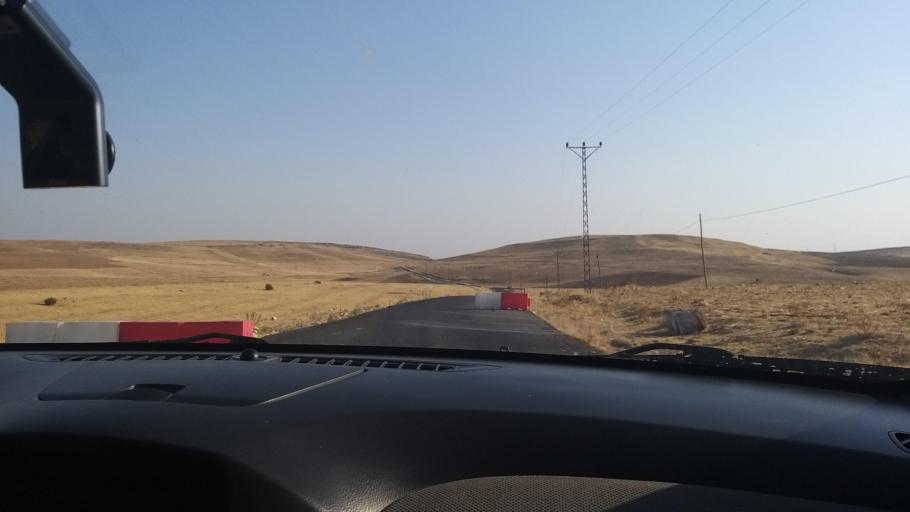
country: TR
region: Diyarbakir
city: Silvan
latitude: 38.1843
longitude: 41.0059
